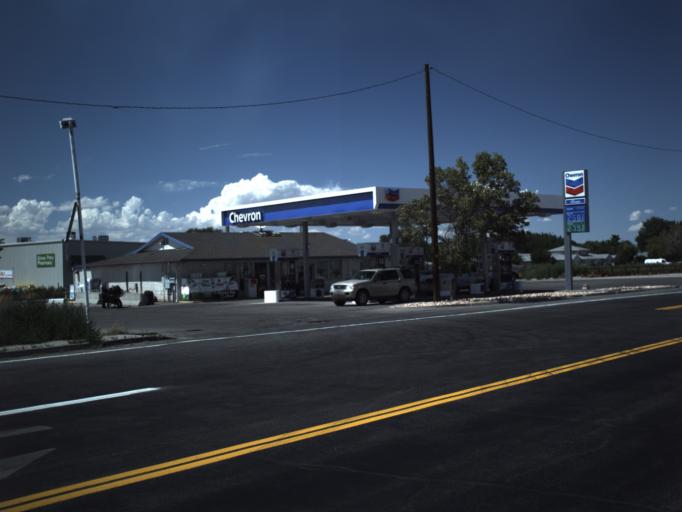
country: US
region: Utah
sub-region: Millard County
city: Delta
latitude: 39.3530
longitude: -112.5636
